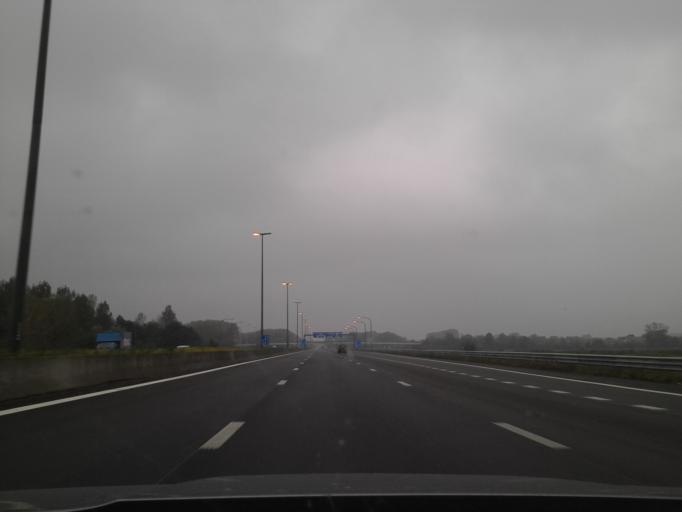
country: BE
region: Wallonia
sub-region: Province du Hainaut
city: Boussu
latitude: 50.4516
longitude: 3.7774
